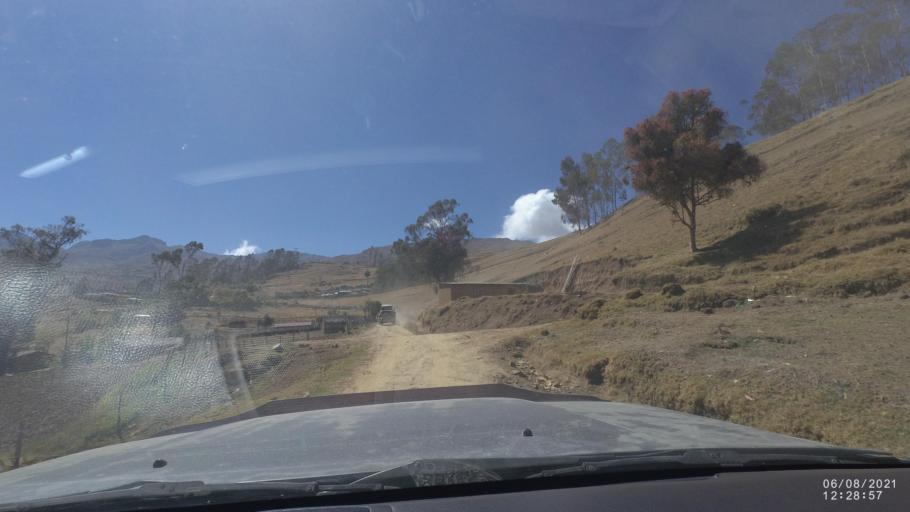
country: BO
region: Cochabamba
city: Colchani
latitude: -16.7929
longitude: -66.6521
